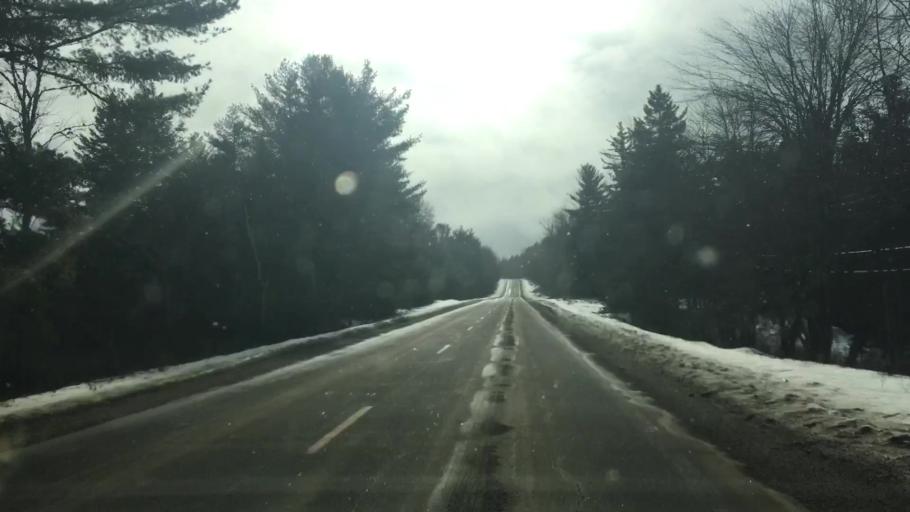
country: US
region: Maine
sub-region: Washington County
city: Calais
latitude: 45.0729
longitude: -67.3319
